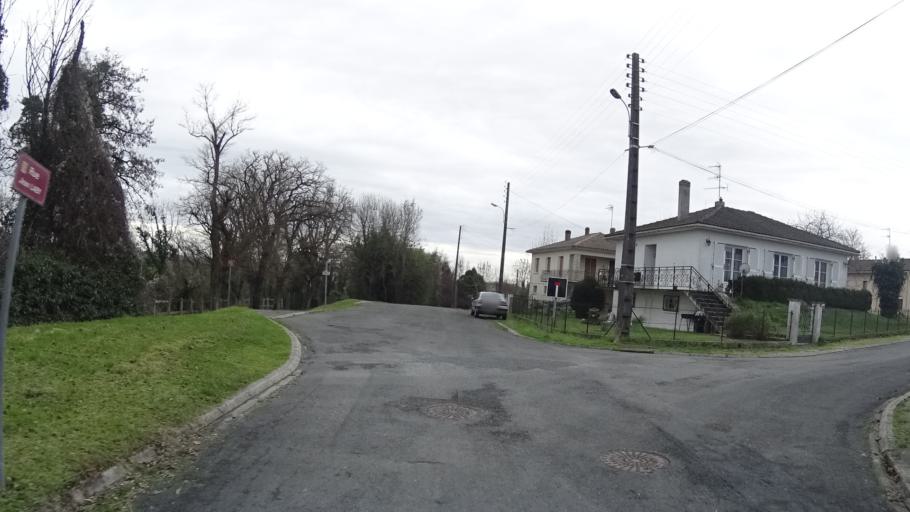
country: FR
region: Aquitaine
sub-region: Departement de la Dordogne
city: Saint-Aulaye
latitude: 45.2044
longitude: 0.1315
